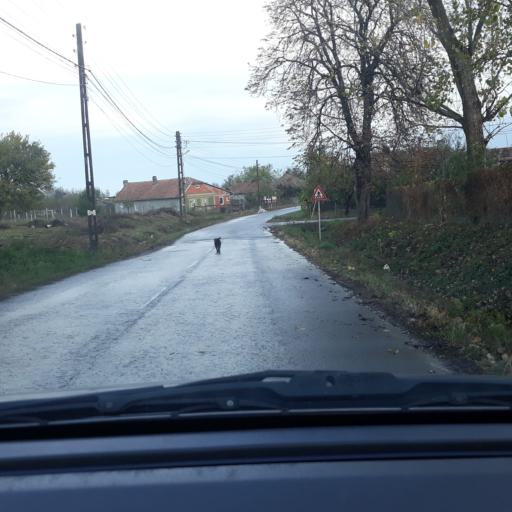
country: RO
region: Bihor
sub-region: Comuna Tarcea
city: Galospetreu
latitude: 47.4849
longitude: 22.2135
